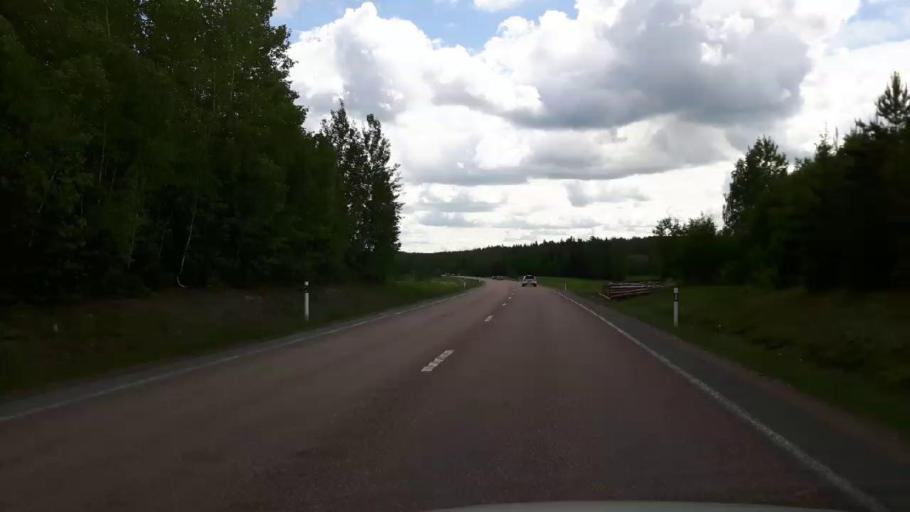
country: SE
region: Dalarna
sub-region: Faluns Kommun
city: Falun
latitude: 60.5030
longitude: 15.7425
